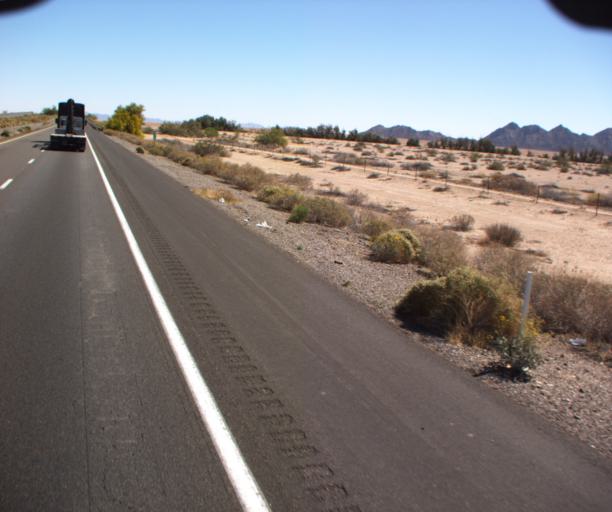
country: US
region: Arizona
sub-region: Yuma County
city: Wellton
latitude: 32.6757
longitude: -114.0557
